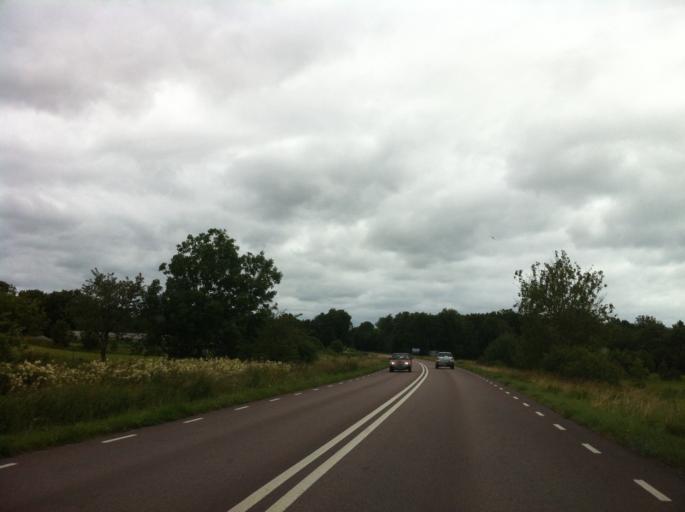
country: SE
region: Kalmar
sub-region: Borgholms Kommun
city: Borgholm
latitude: 57.1749
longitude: 17.0274
